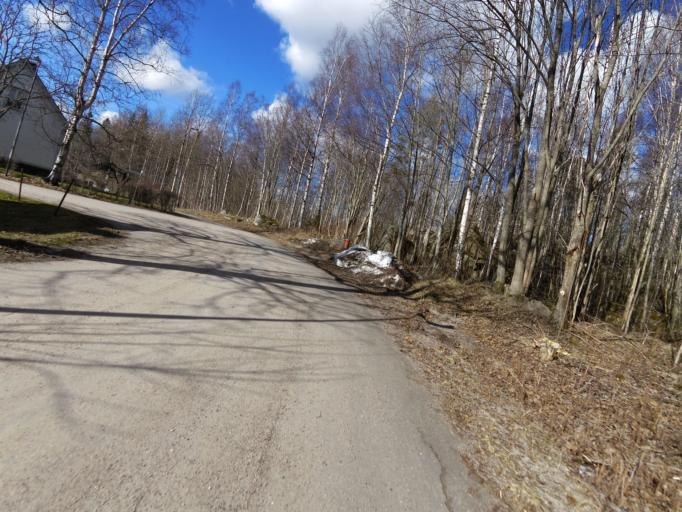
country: SE
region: Gaevleborg
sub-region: Hofors Kommun
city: Hofors
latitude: 60.5438
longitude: 16.3111
